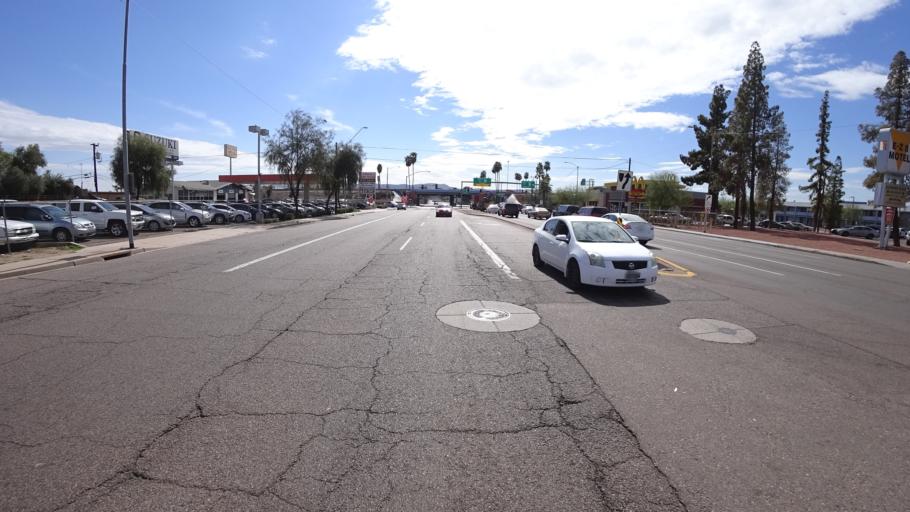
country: US
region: Arizona
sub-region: Maricopa County
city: Phoenix
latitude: 33.4303
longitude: -112.0651
